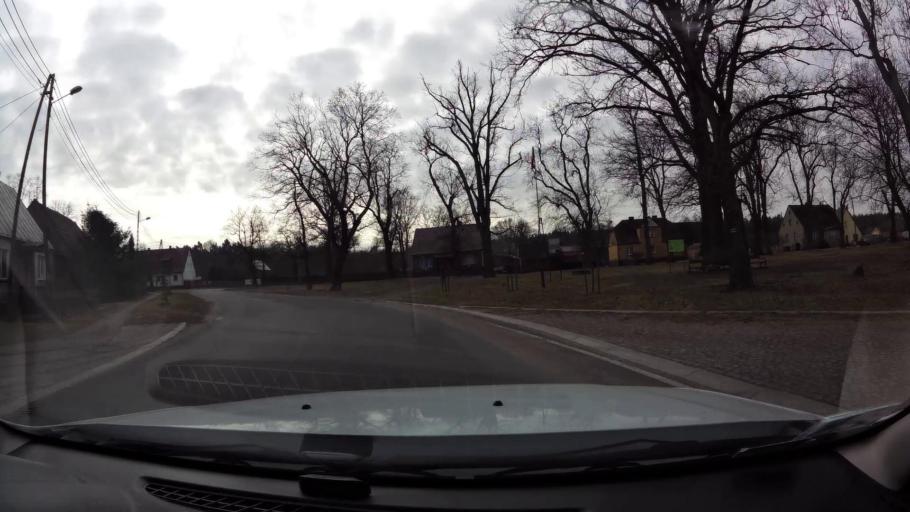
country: PL
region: West Pomeranian Voivodeship
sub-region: Powiat mysliborski
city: Debno
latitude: 52.7065
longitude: 14.6463
